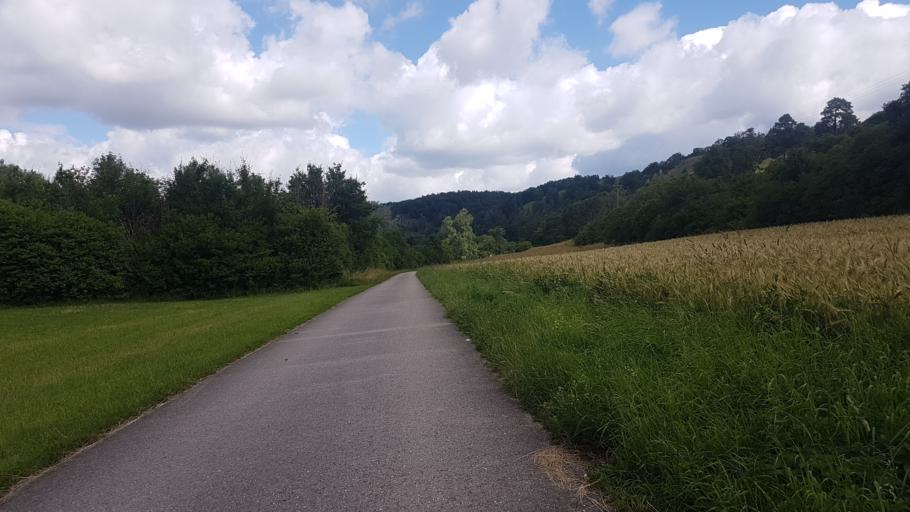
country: DE
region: Bavaria
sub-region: Upper Bavaria
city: Walting
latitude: 48.9284
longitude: 11.3388
